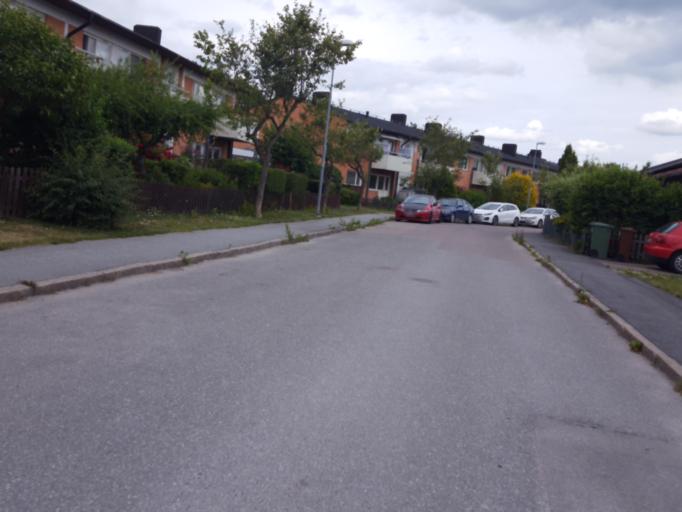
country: SE
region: Uppsala
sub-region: Uppsala Kommun
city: Uppsala
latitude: 59.8612
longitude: 17.6812
